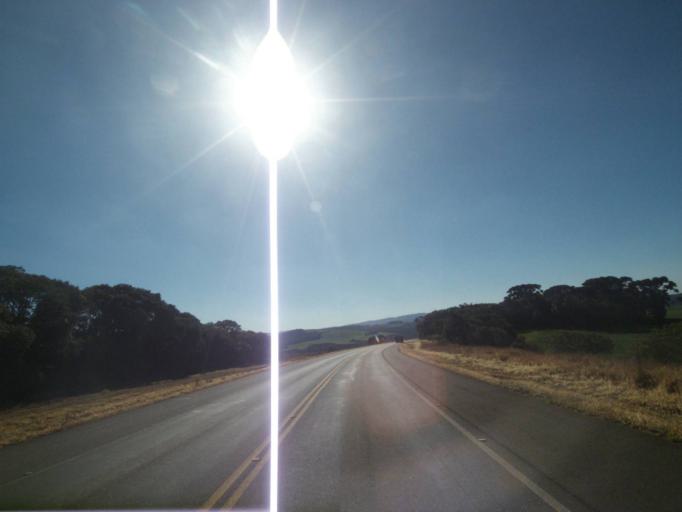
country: BR
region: Parana
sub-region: Tibagi
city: Tibagi
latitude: -24.6728
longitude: -50.4525
